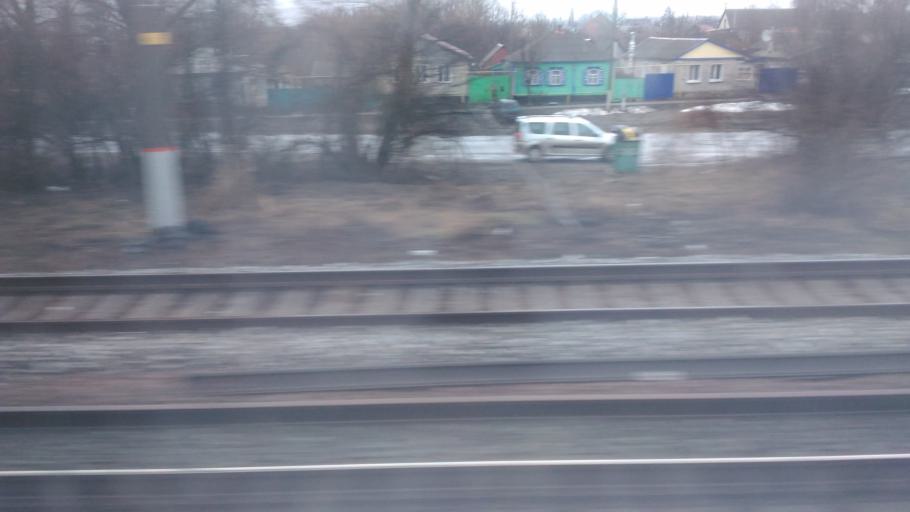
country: RU
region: Voronezj
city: Imeni Pervogo Maya
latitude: 50.7143
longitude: 39.4279
